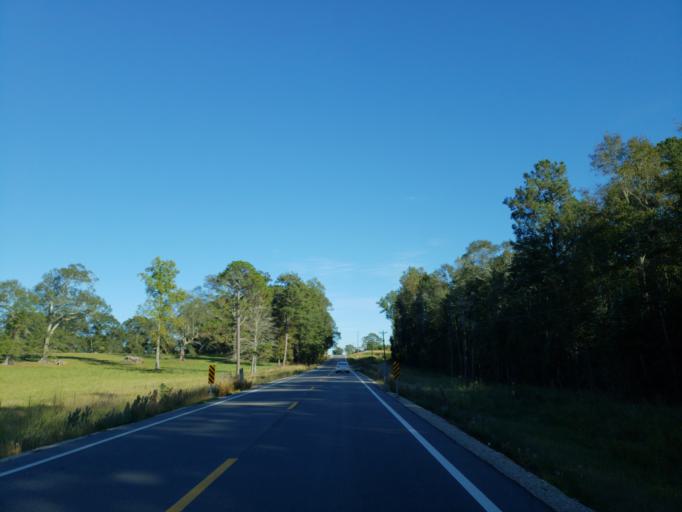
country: US
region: Mississippi
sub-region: Perry County
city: Richton
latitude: 31.3614
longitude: -89.0439
